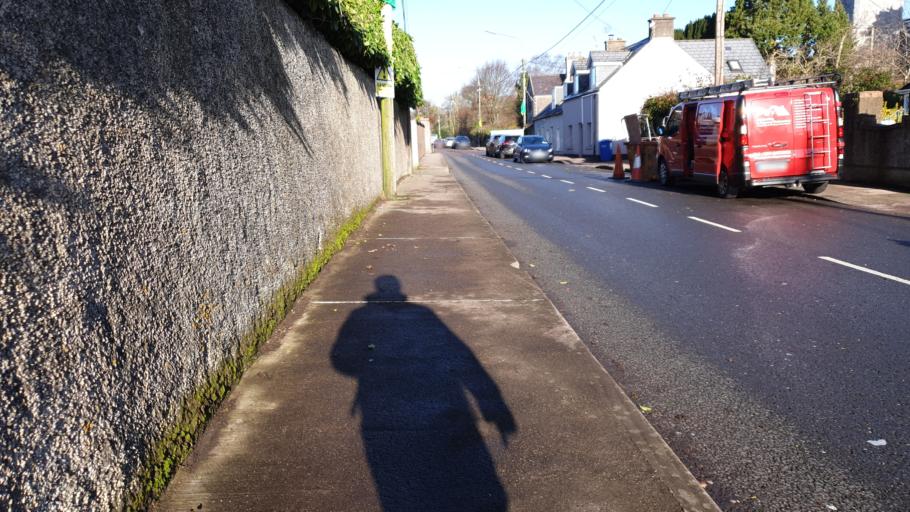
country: IE
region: Munster
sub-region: County Cork
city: Cork
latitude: 51.8947
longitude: -8.4203
